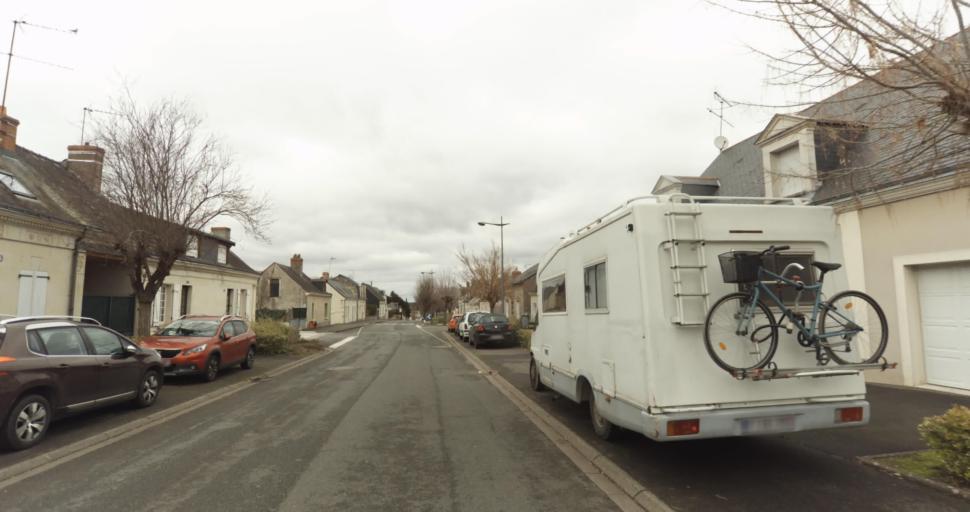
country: FR
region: Pays de la Loire
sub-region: Departement de Maine-et-Loire
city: Jumelles
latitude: 47.3780
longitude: -0.1059
